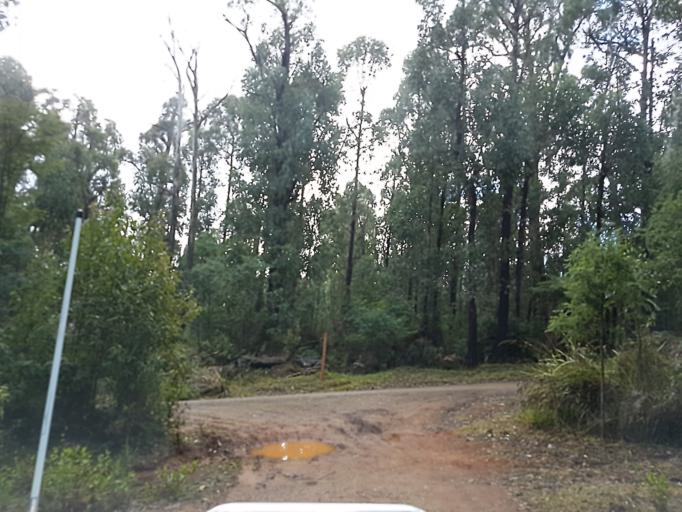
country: AU
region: Victoria
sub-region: Yarra Ranges
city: Millgrove
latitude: -37.5392
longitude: 145.7389
